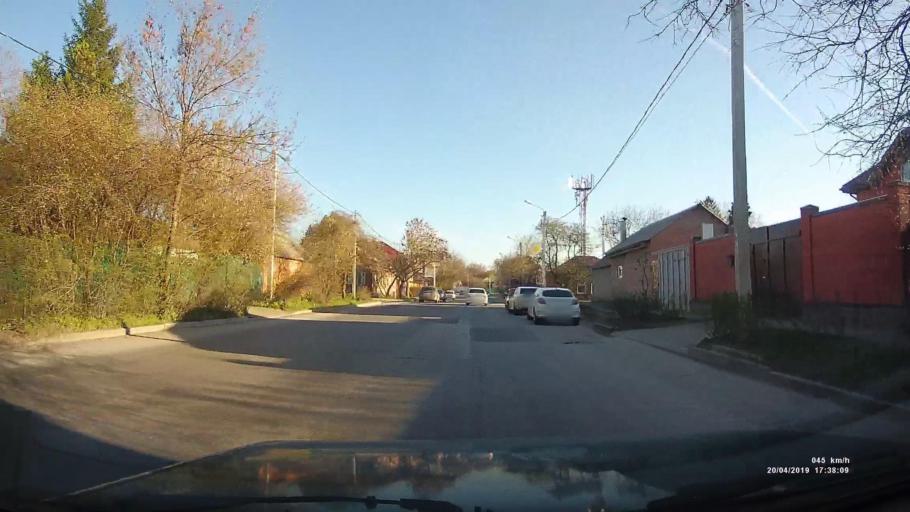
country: RU
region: Rostov
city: Imeni Chkalova
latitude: 47.2481
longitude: 39.7966
